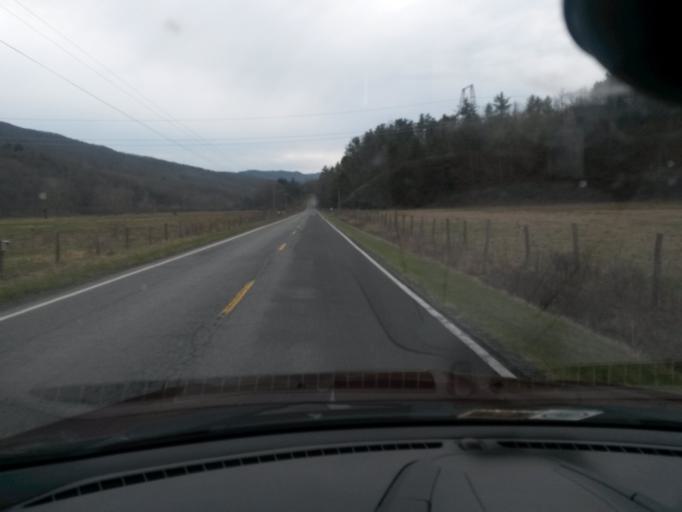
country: US
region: Virginia
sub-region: Highland County
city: Monterey
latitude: 38.2502
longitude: -79.6785
